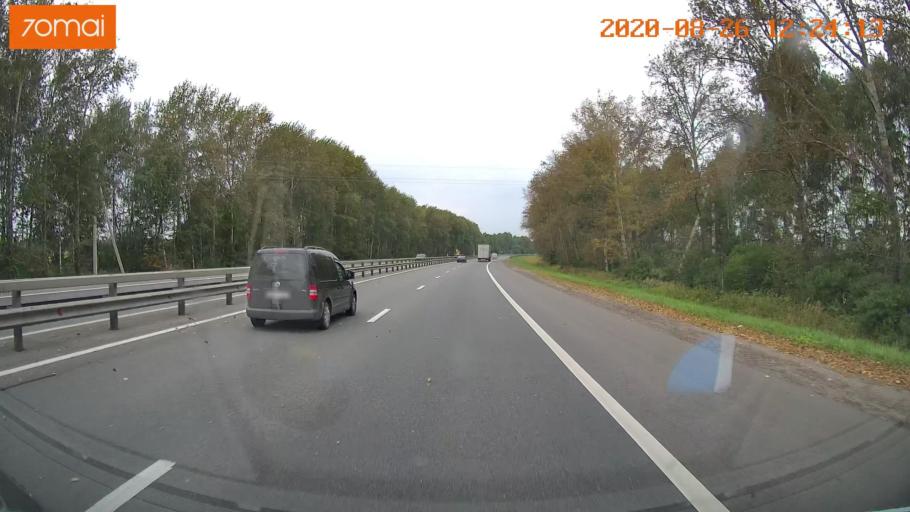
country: RU
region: Rjazan
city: Murmino
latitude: 54.5113
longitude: 39.8962
